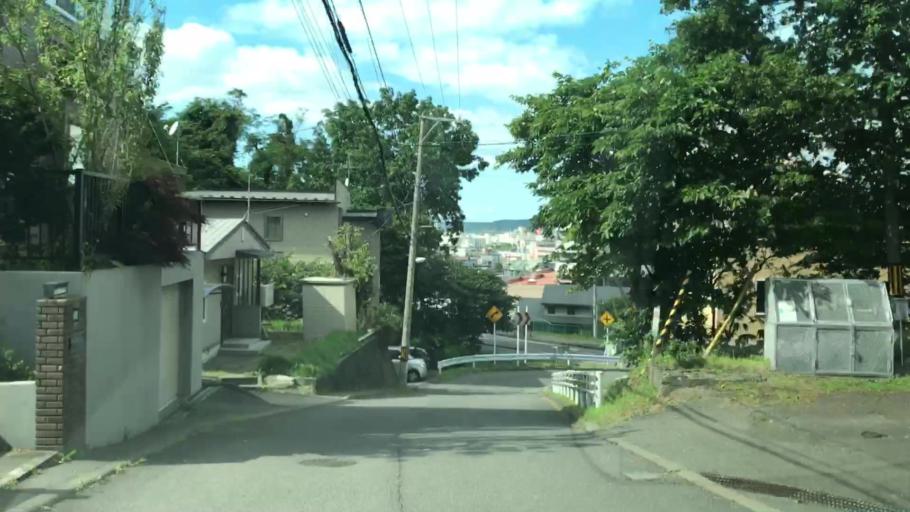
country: JP
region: Hokkaido
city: Muroran
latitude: 42.3119
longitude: 140.9764
